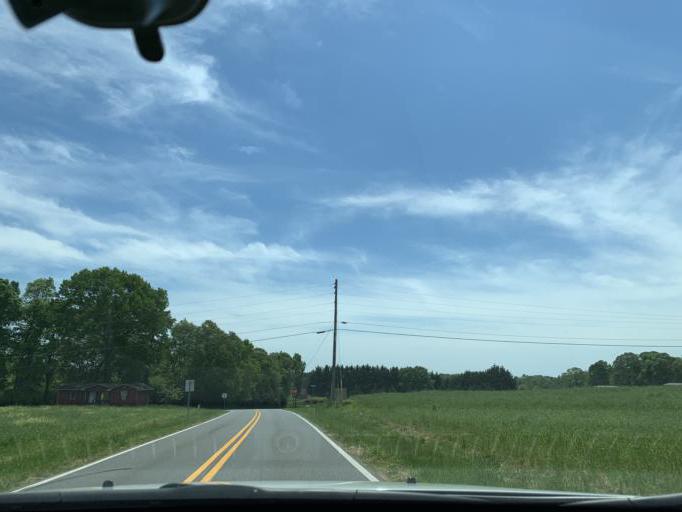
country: US
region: Georgia
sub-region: Hall County
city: Flowery Branch
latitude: 34.2809
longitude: -84.0222
